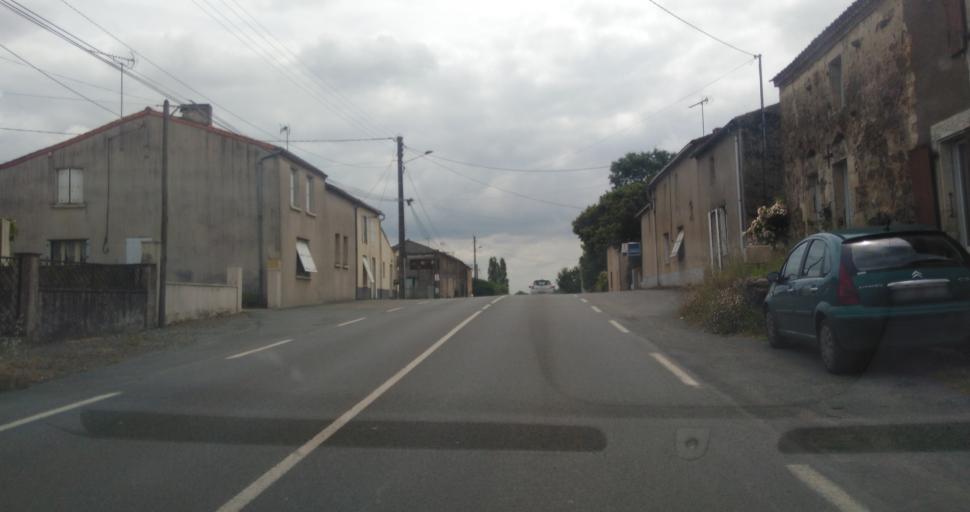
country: FR
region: Pays de la Loire
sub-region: Departement de la Vendee
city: Bournezeau
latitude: 46.6165
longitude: -1.1503
